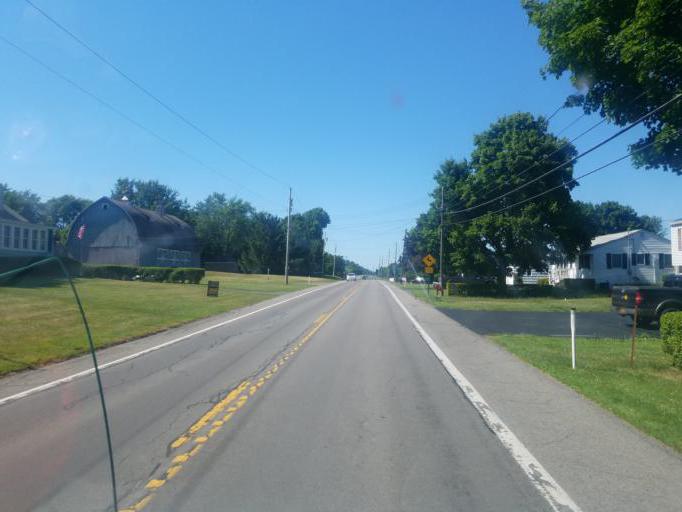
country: US
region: New York
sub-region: Wayne County
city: Newark
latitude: 43.0206
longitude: -77.0944
